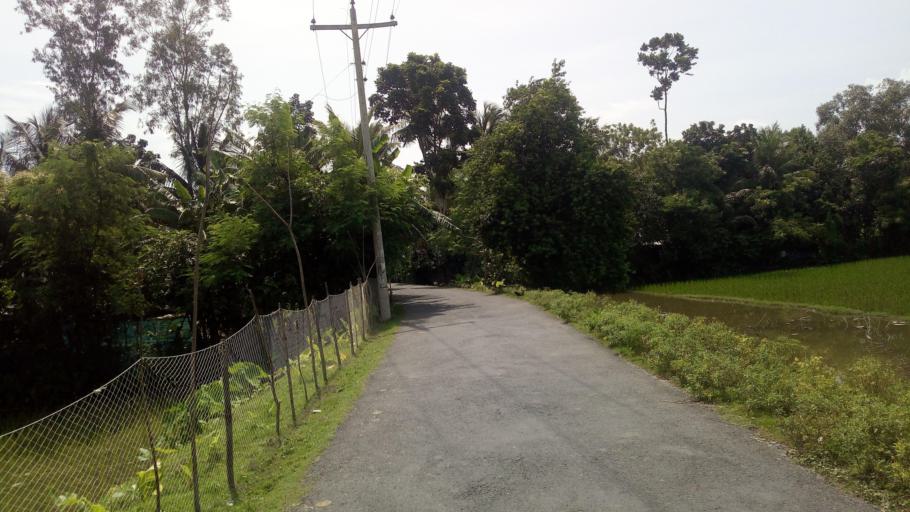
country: BD
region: Khulna
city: Phultala
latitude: 22.5741
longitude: 89.4556
